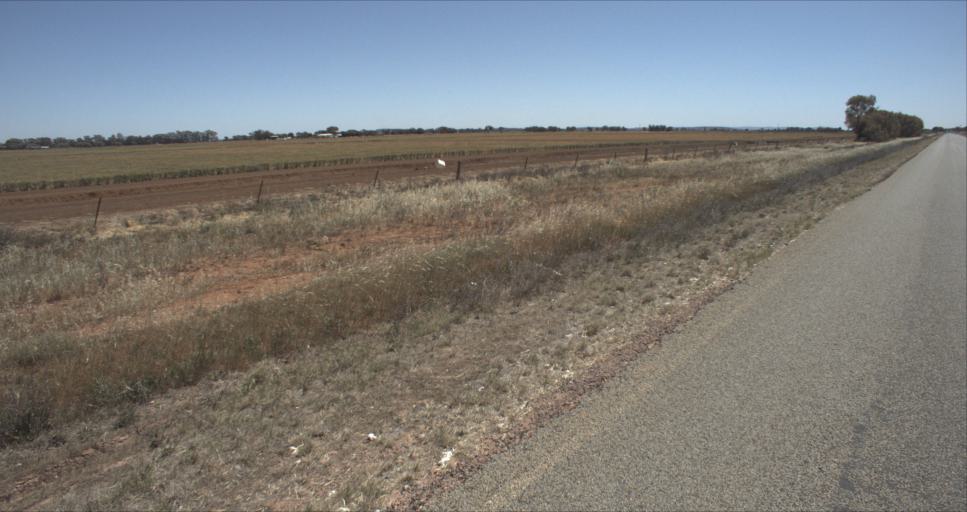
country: AU
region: New South Wales
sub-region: Leeton
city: Leeton
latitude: -34.4625
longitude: 146.2939
